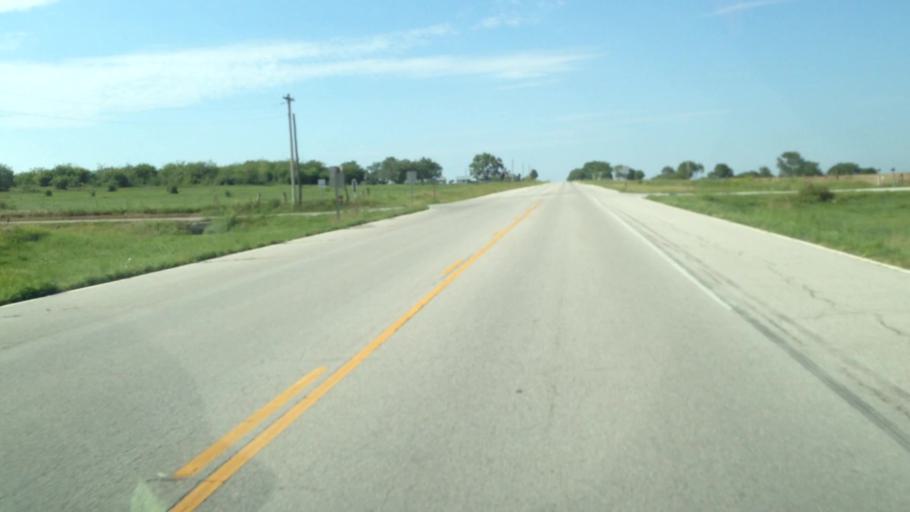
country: US
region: Kansas
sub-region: Neosho County
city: Erie
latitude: 37.4705
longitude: -95.2693
